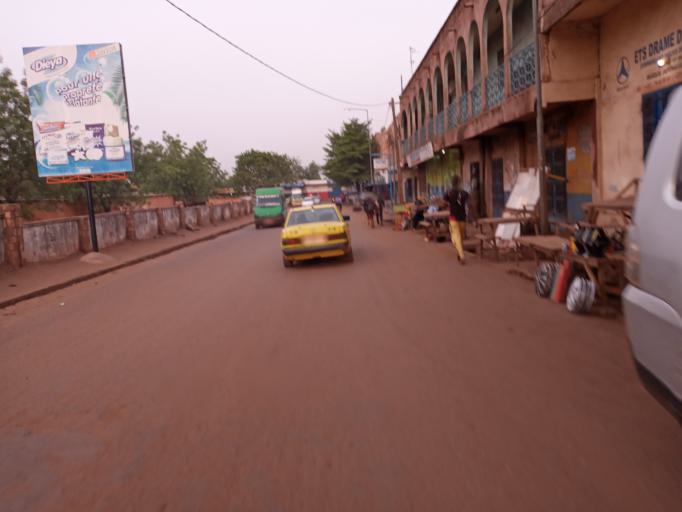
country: ML
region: Bamako
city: Bamako
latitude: 12.6608
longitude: -7.9826
